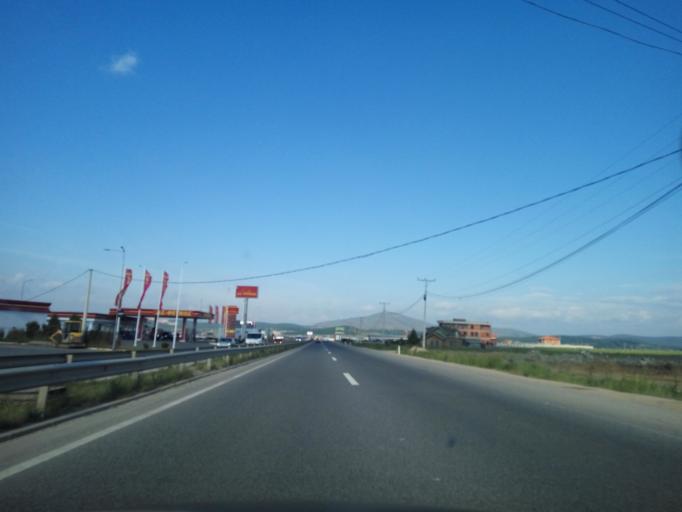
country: XK
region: Pristina
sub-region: Komuna e Drenasit
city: Glogovac
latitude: 42.5753
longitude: 20.8760
